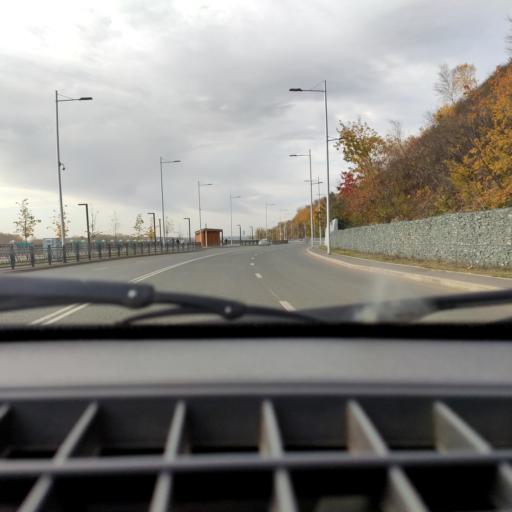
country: RU
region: Bashkortostan
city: Ufa
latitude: 54.7118
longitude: 55.9515
